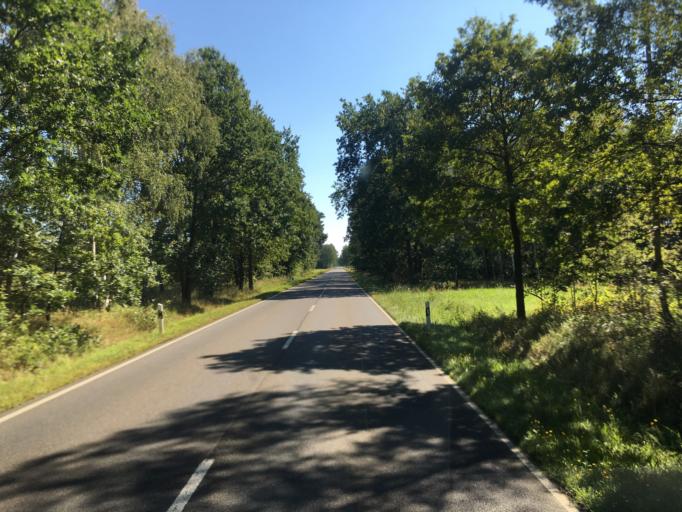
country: DE
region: Brandenburg
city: Welzow
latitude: 51.5448
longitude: 14.1689
